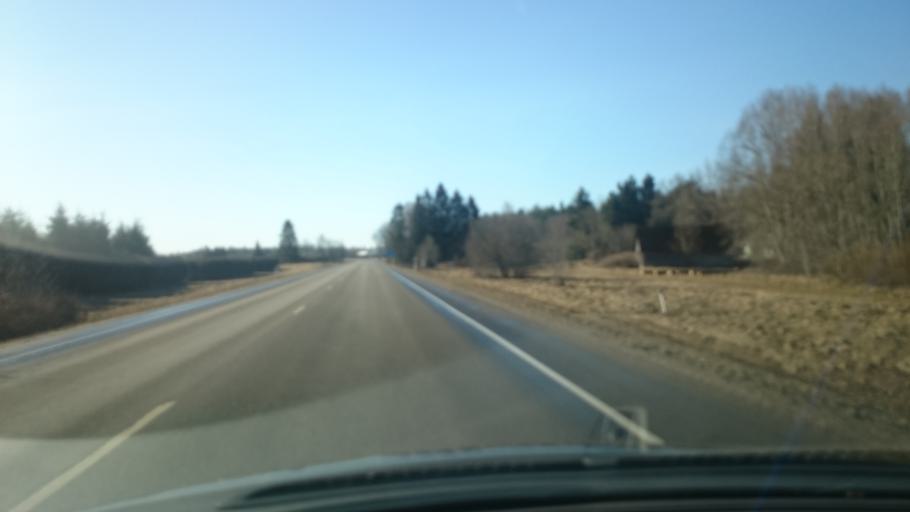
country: EE
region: Raplamaa
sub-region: Kohila vald
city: Kohila
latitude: 59.2560
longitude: 24.7410
